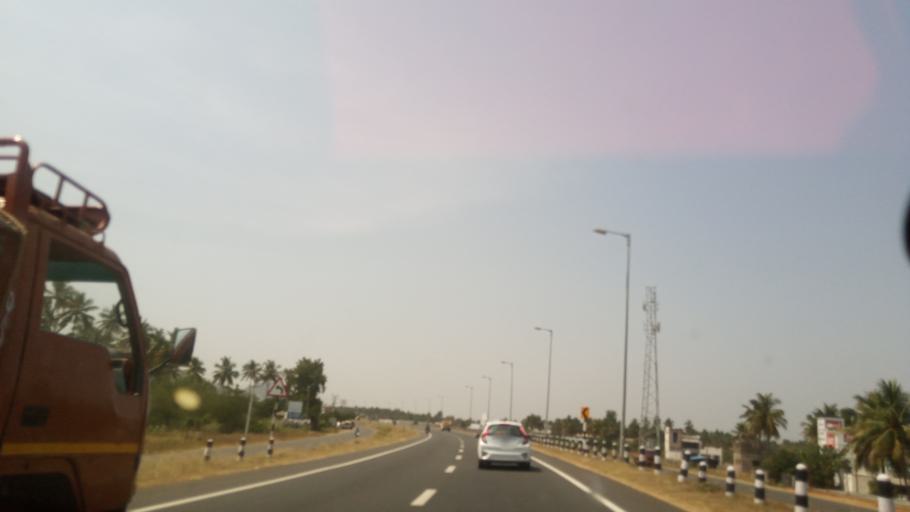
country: IN
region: Tamil Nadu
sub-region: Salem
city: Salem
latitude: 11.6641
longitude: 78.2358
